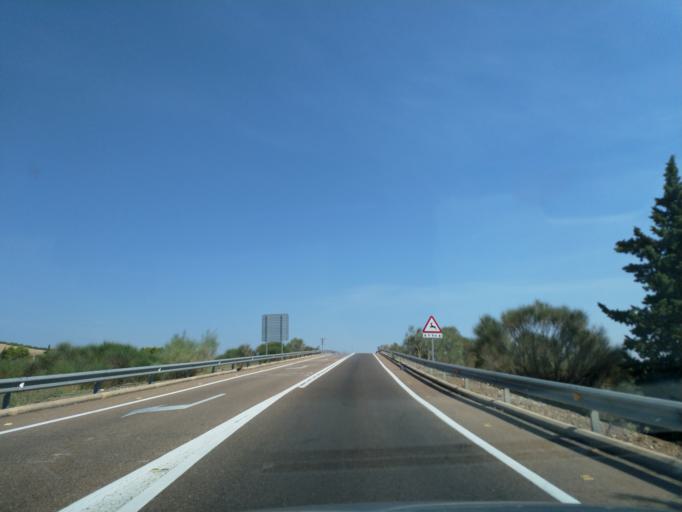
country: ES
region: Extremadura
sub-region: Provincia de Badajoz
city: Merida
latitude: 38.9411
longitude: -6.3430
